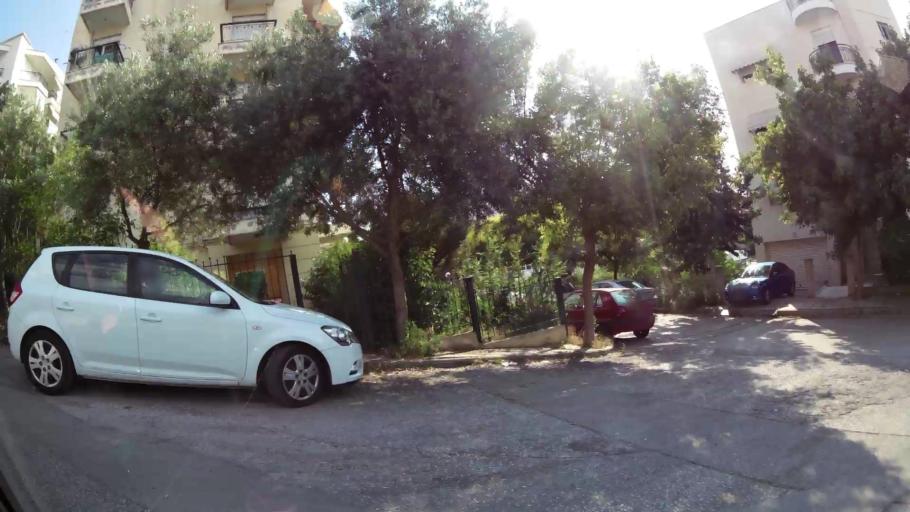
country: GR
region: Central Macedonia
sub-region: Nomos Thessalonikis
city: Polichni
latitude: 40.6610
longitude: 22.9548
